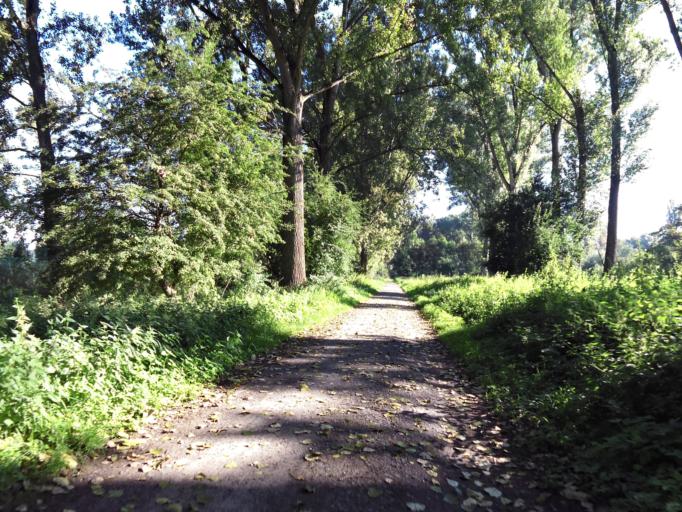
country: DE
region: Hesse
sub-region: Regierungsbezirk Darmstadt
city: Gross-Rohrheim
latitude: 49.7364
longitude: 8.4549
